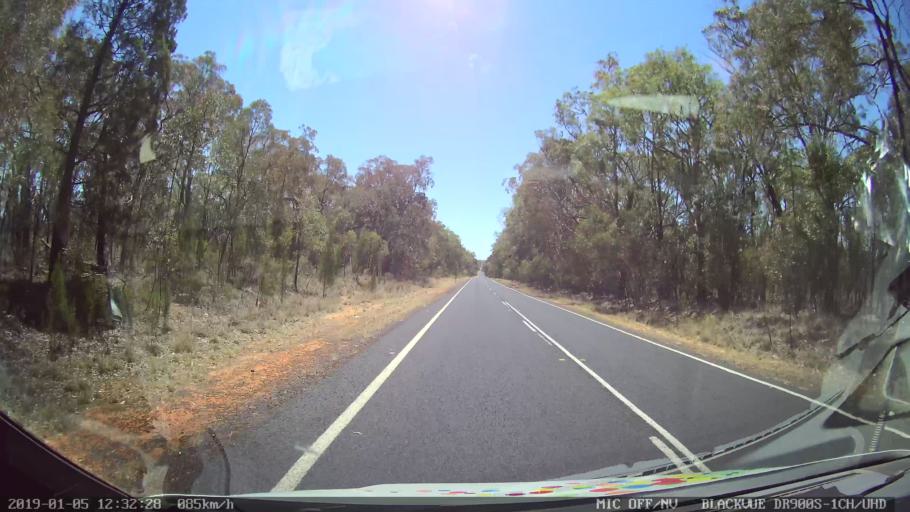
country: AU
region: New South Wales
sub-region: Warrumbungle Shire
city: Coonabarabran
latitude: -31.2172
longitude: 149.3801
